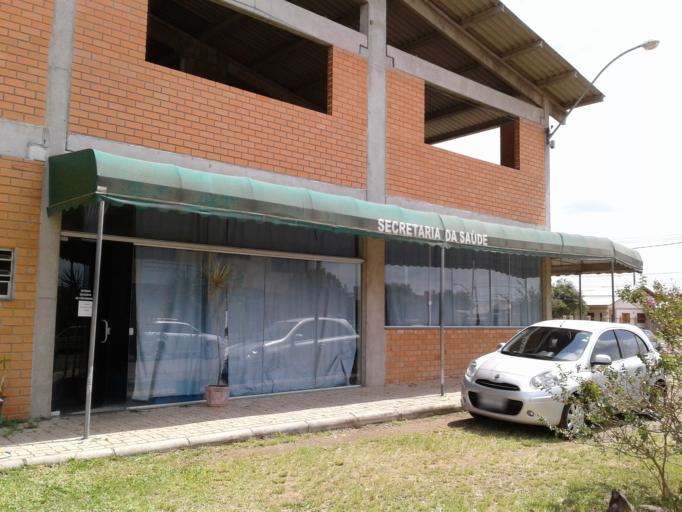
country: BR
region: Rio Grande do Sul
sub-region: Gravatai
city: Gravatai
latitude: -29.8812
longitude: -50.7822
